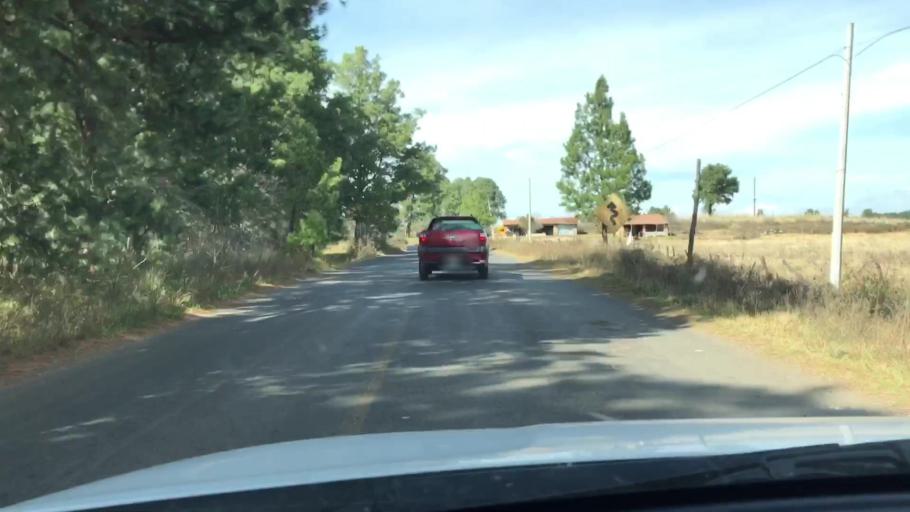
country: MX
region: Jalisco
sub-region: Amacueca
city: Tepec
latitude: 20.0795
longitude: -103.7116
